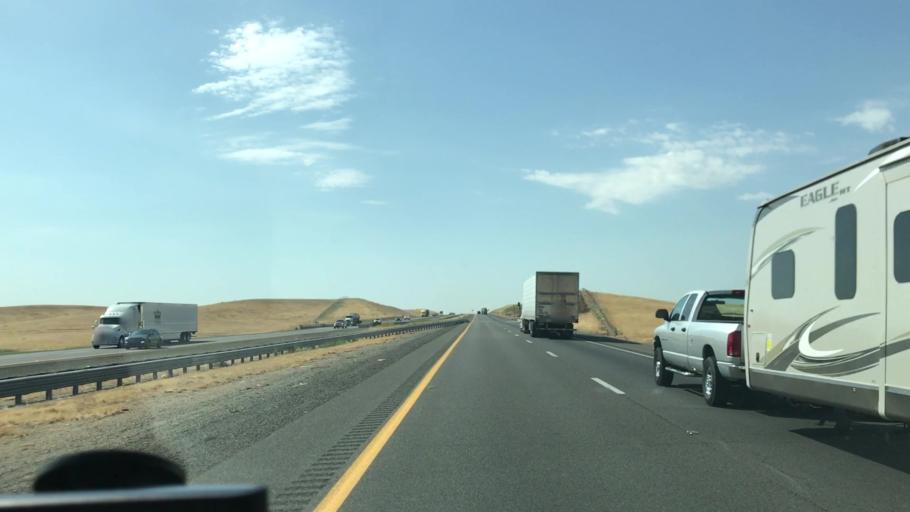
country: US
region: California
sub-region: Merced County
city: Gustine
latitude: 37.1787
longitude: -121.0643
